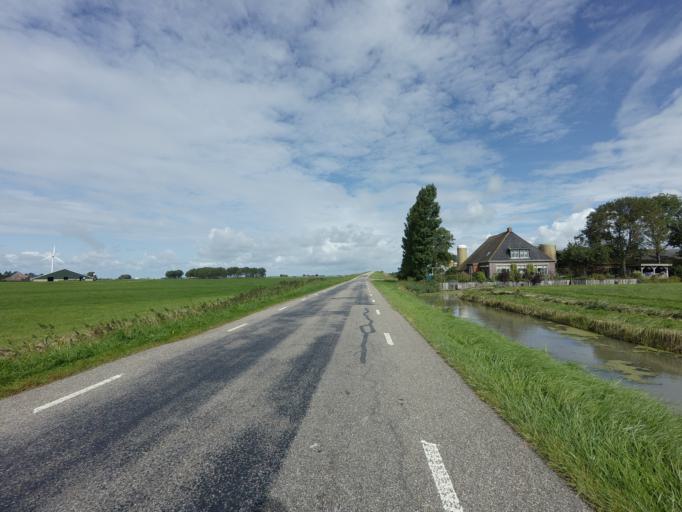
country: NL
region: Friesland
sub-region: Sudwest Fryslan
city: Makkum
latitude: 53.0900
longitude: 5.4208
